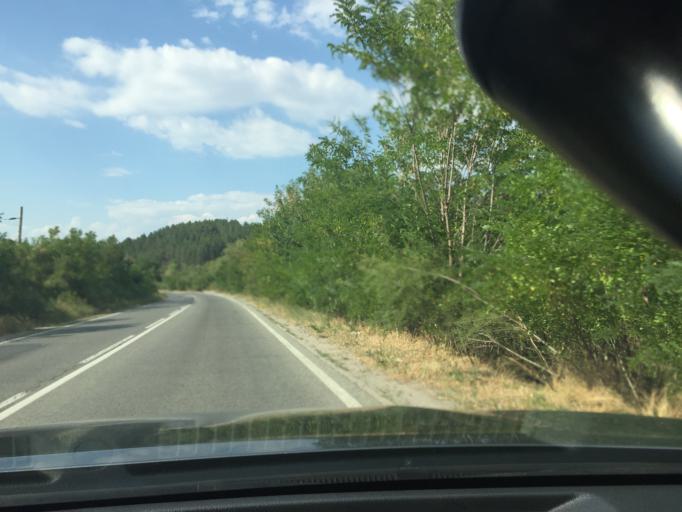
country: BG
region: Kyustendil
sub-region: Obshtina Kocherinovo
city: Kocherinovo
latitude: 42.1024
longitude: 23.0398
